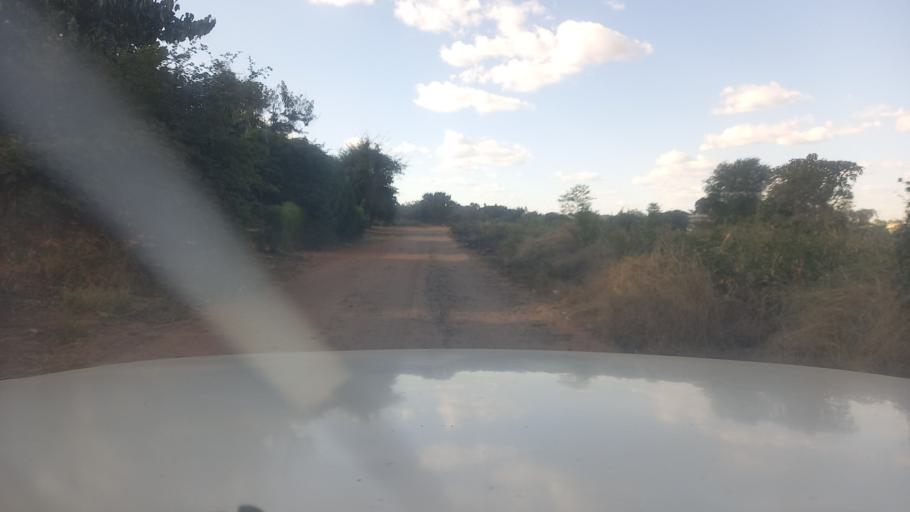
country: ZM
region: Southern
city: Livingstone
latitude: -17.8300
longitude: 25.8677
